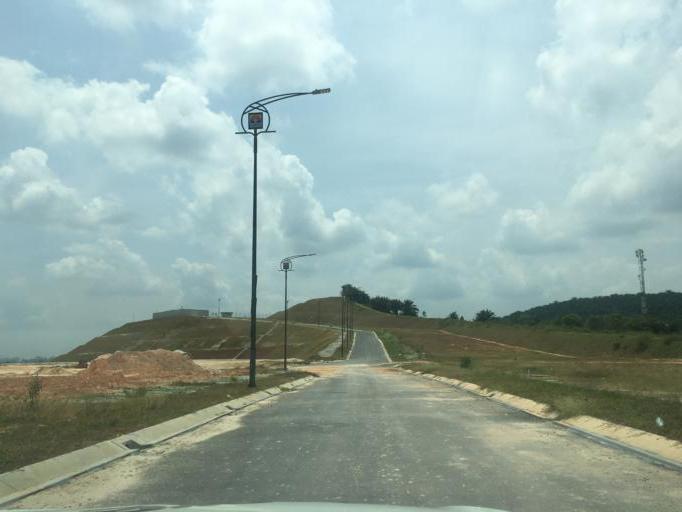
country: MY
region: Putrajaya
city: Putrajaya
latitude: 2.8458
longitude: 101.7109
